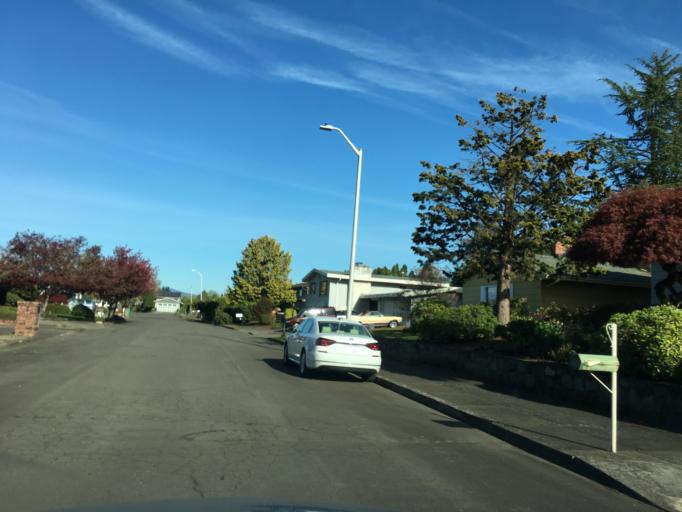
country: US
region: Oregon
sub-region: Multnomah County
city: Fairview
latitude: 45.5484
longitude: -122.5154
